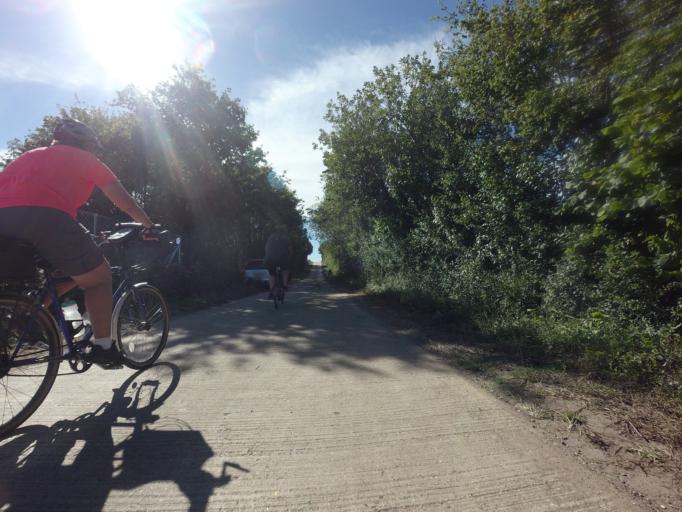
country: GB
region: England
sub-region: Kent
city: Birchington-on-Sea
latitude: 51.3610
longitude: 1.2274
